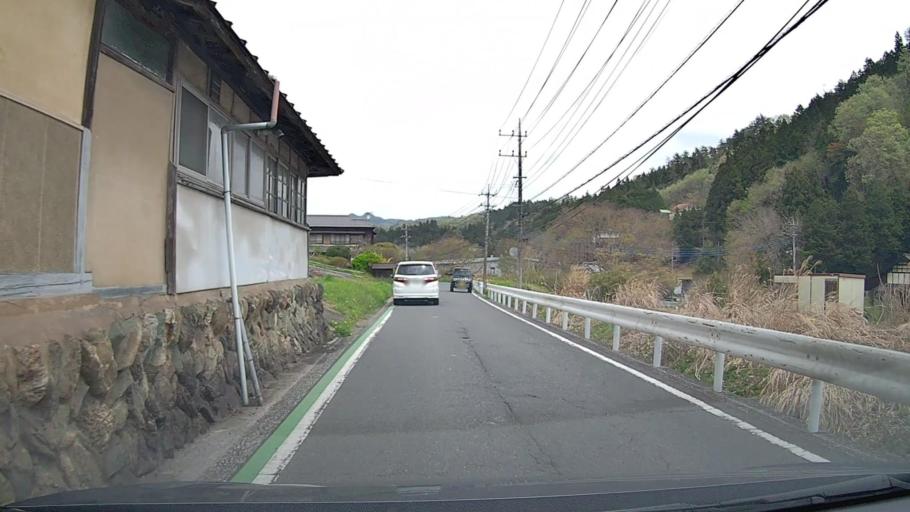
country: JP
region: Saitama
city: Chichibu
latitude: 36.0480
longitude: 139.1317
